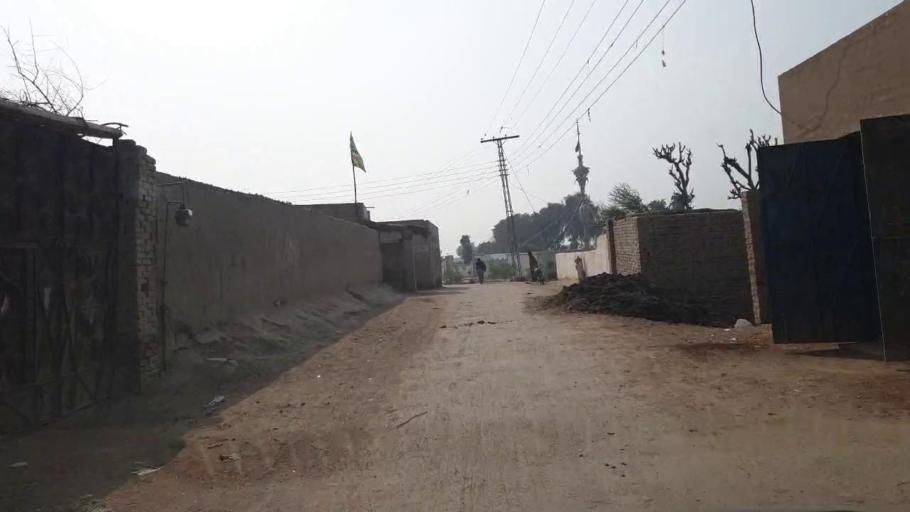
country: PK
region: Sindh
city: Bhit Shah
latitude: 25.8384
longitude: 68.4641
